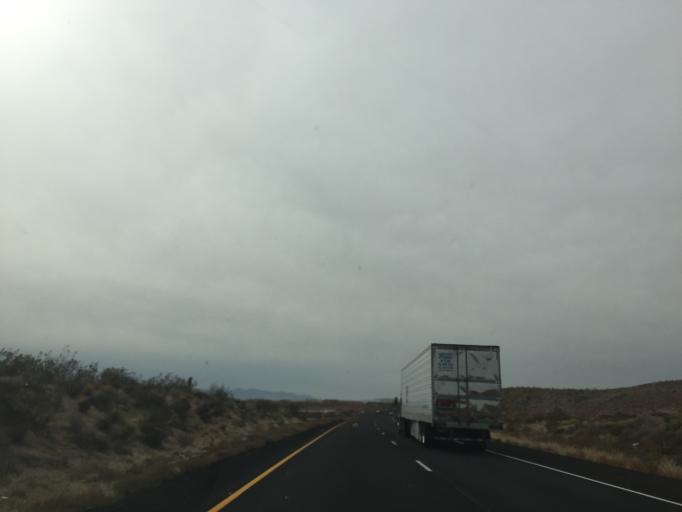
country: US
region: Utah
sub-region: Washington County
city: Washington
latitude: 37.1802
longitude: -113.4185
